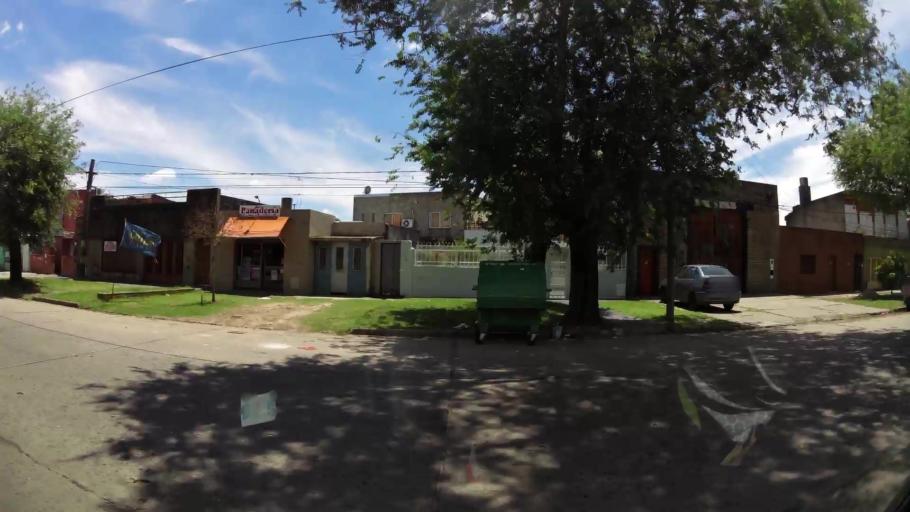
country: AR
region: Santa Fe
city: Gobernador Galvez
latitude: -32.9902
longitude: -60.6310
